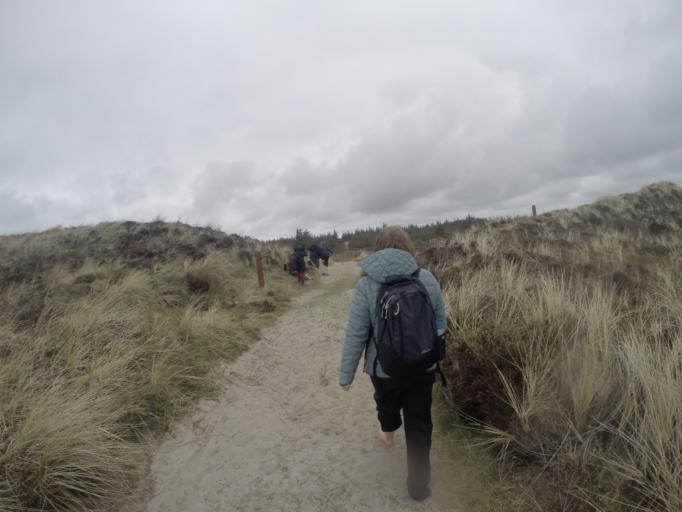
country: DK
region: North Denmark
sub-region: Thisted Kommune
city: Hurup
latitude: 56.8979
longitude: 8.3362
